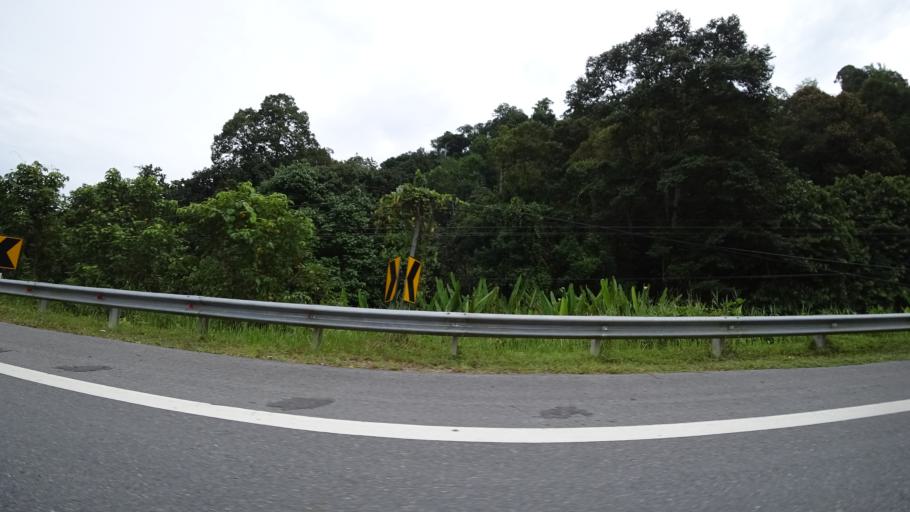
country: MY
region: Sarawak
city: Limbang
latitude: 4.6639
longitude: 114.9400
